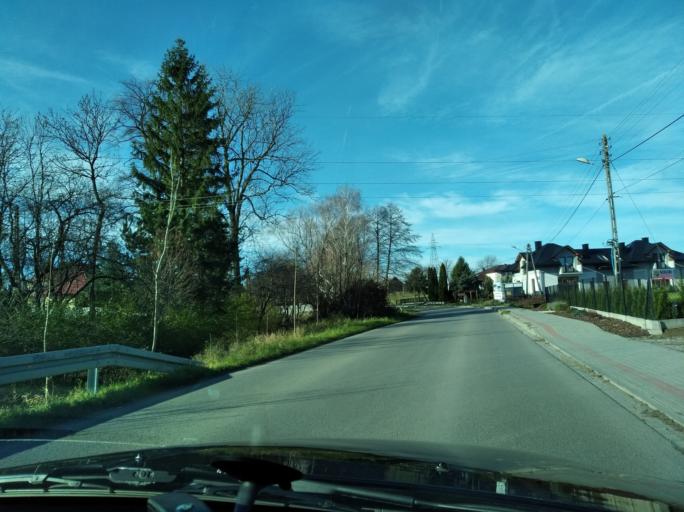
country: PL
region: Subcarpathian Voivodeship
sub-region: Powiat rzeszowski
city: Kielanowka
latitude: 50.0107
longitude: 21.9344
